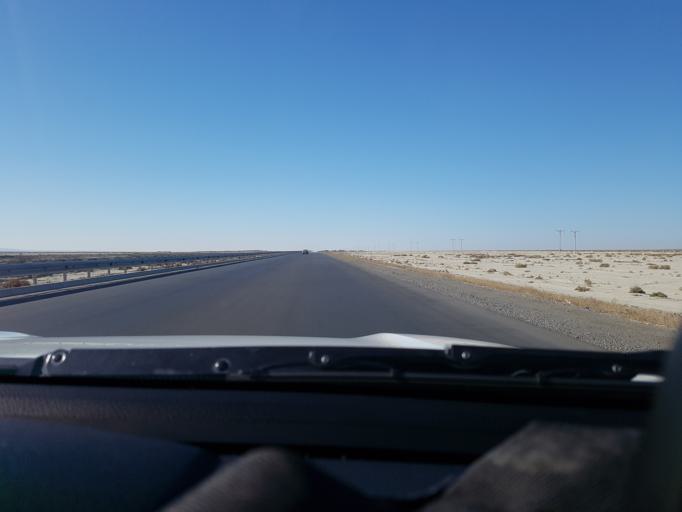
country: TM
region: Balkan
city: Gazanjyk
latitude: 39.2520
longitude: 55.1012
